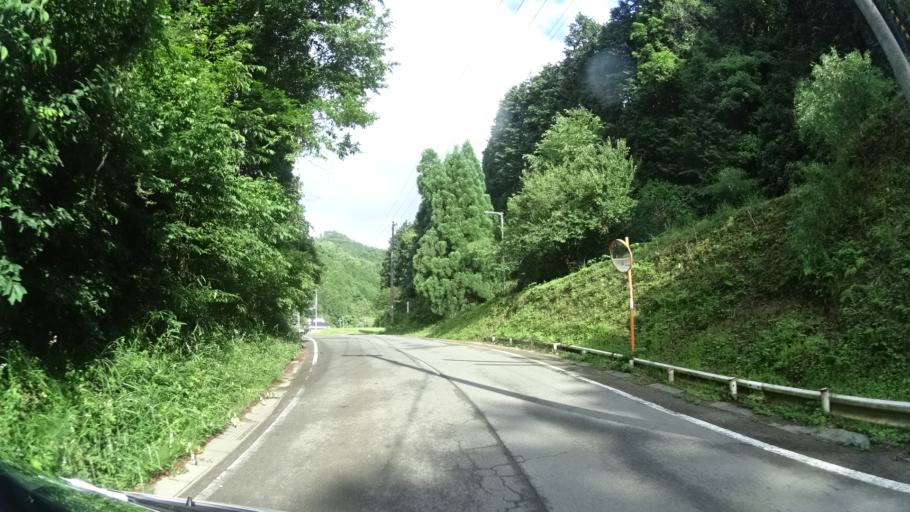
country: JP
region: Kyoto
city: Ayabe
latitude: 35.3716
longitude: 135.2850
